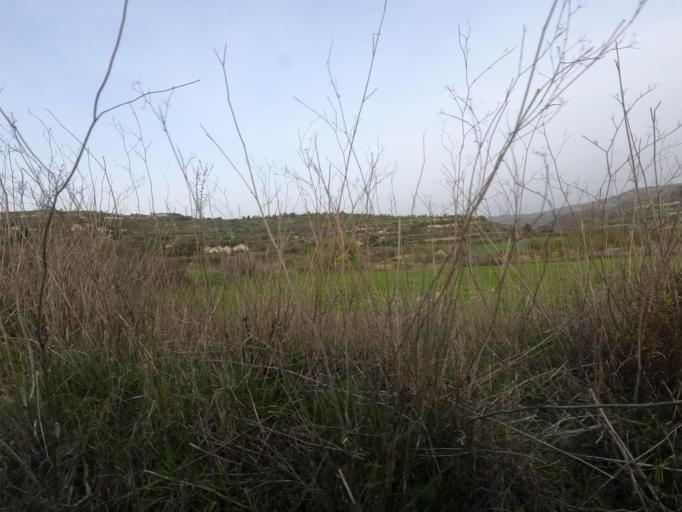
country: CY
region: Pafos
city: Mesogi
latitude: 34.8654
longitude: 32.4961
